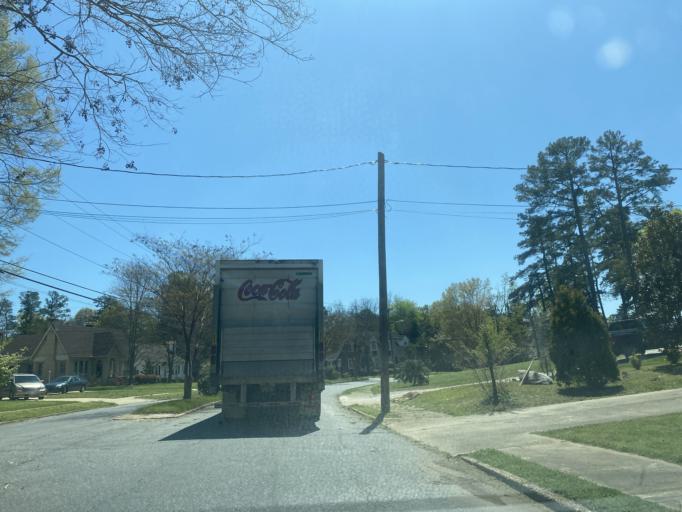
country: US
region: South Carolina
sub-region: Cherokee County
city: Gaffney
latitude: 35.0609
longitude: -81.6460
